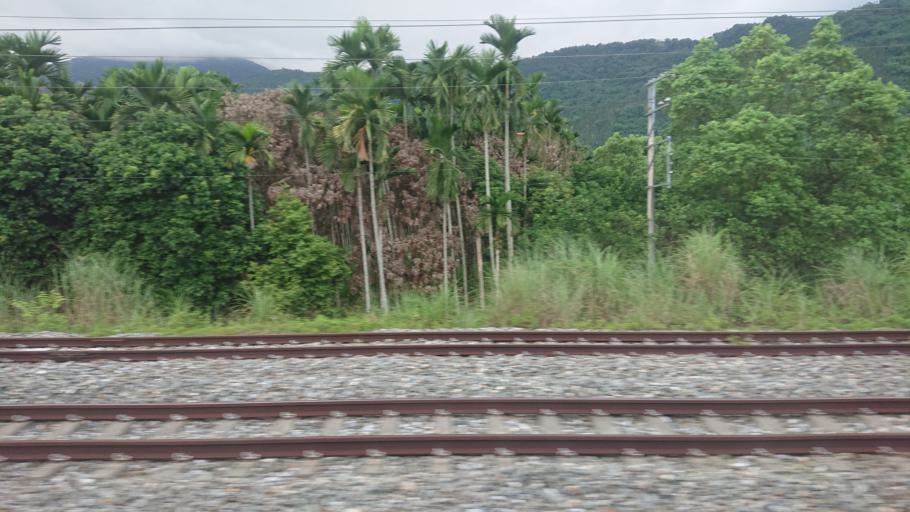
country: TW
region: Taiwan
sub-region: Hualien
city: Hualian
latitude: 23.6644
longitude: 121.4202
